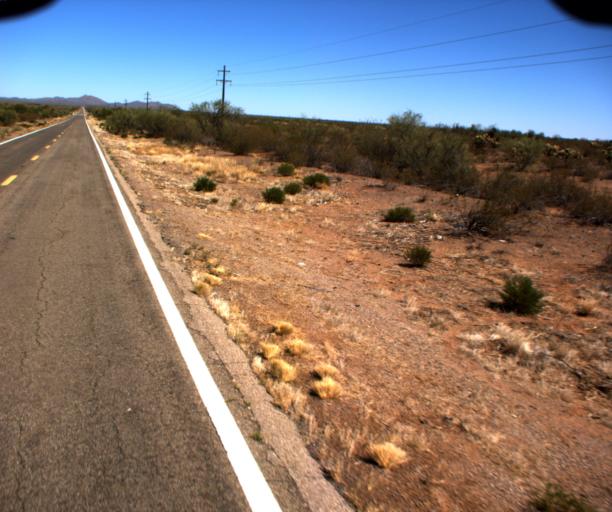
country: US
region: Arizona
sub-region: Pima County
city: Sells
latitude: 32.0853
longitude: -112.0536
